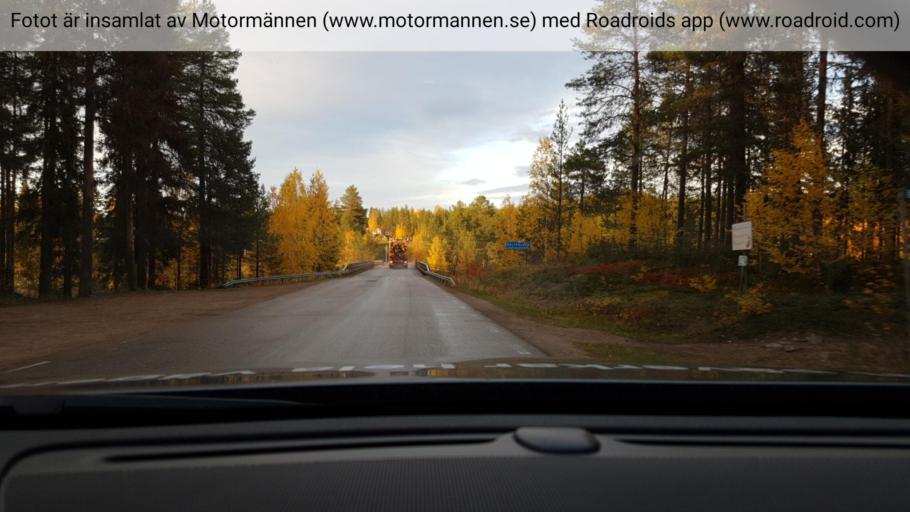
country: SE
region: Norrbotten
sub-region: Overkalix Kommun
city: OEverkalix
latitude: 66.6501
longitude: 22.7112
